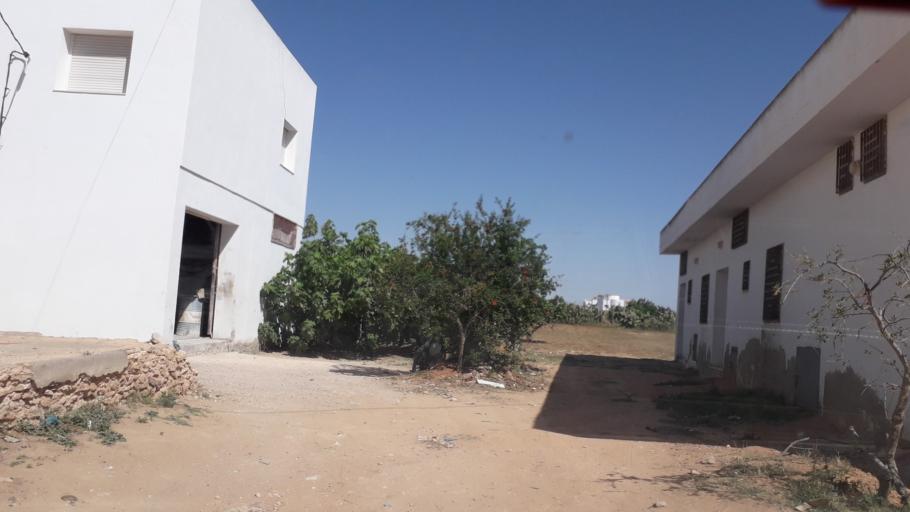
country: TN
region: Safaqis
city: Al Qarmadah
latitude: 34.8104
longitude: 10.7706
